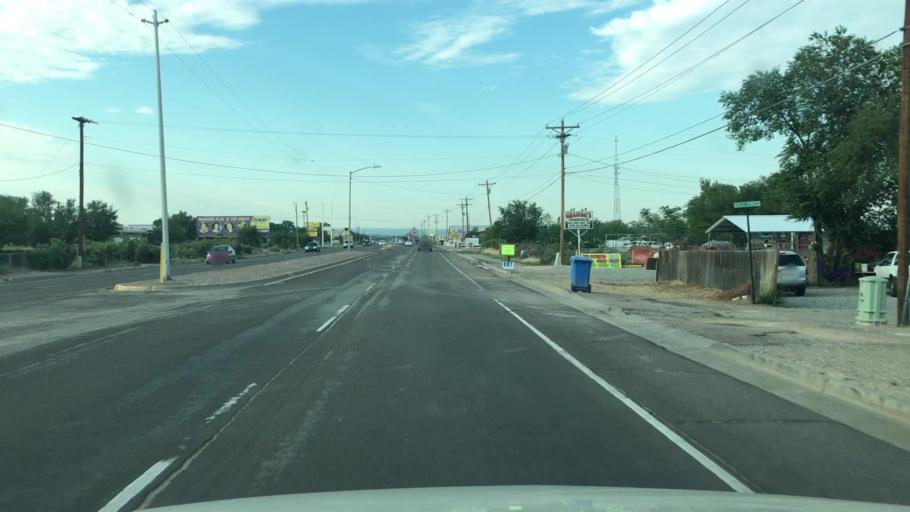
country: US
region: New Mexico
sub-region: Rio Arriba County
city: Ohkay Owingeh
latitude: 36.0223
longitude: -106.0640
